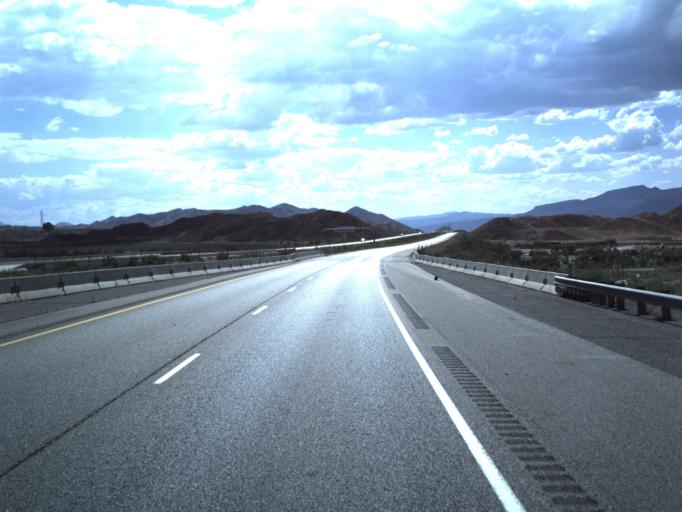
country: US
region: Utah
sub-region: Sevier County
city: Salina
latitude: 38.9154
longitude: -111.8833
